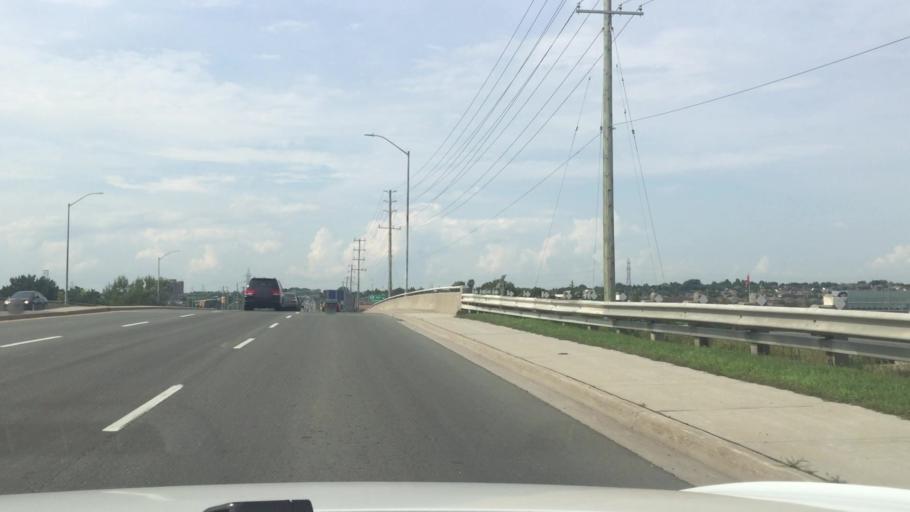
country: CA
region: Ontario
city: Oshawa
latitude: 43.8674
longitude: -78.9038
